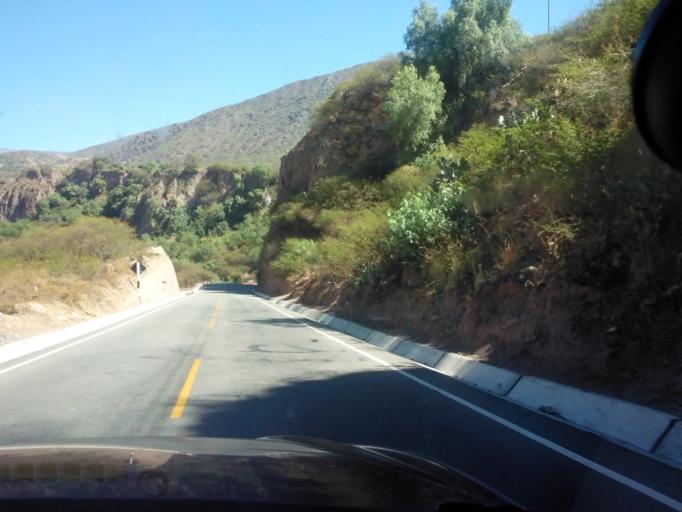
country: PE
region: Ayacucho
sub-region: Provincia de Huamanga
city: Ocros
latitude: -13.4230
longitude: -73.8533
